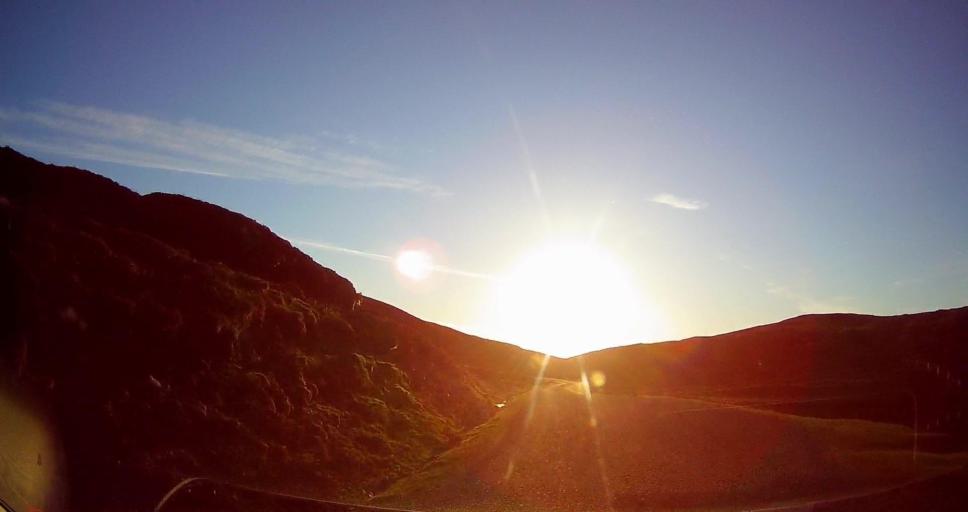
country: GB
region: Scotland
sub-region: Shetland Islands
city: Lerwick
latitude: 60.4440
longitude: -1.4091
